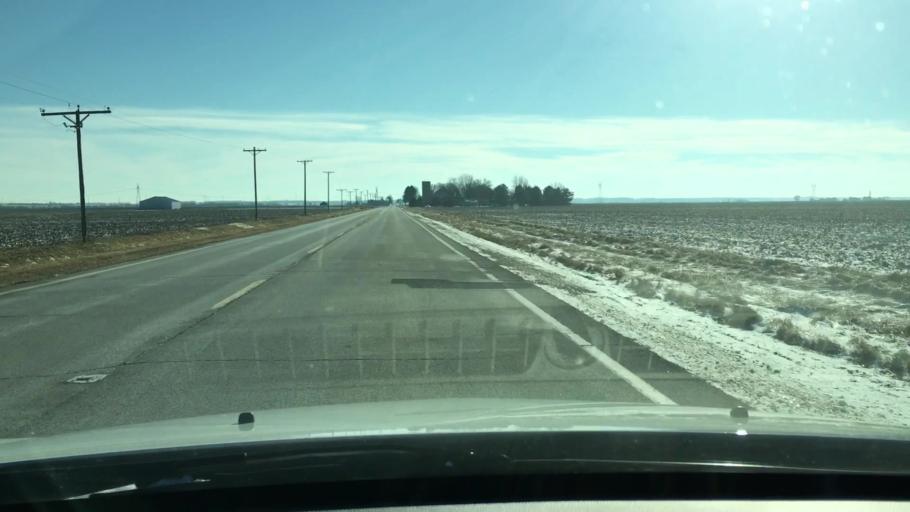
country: US
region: Illinois
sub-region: Ogle County
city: Rochelle
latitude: 41.8117
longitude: -89.0834
